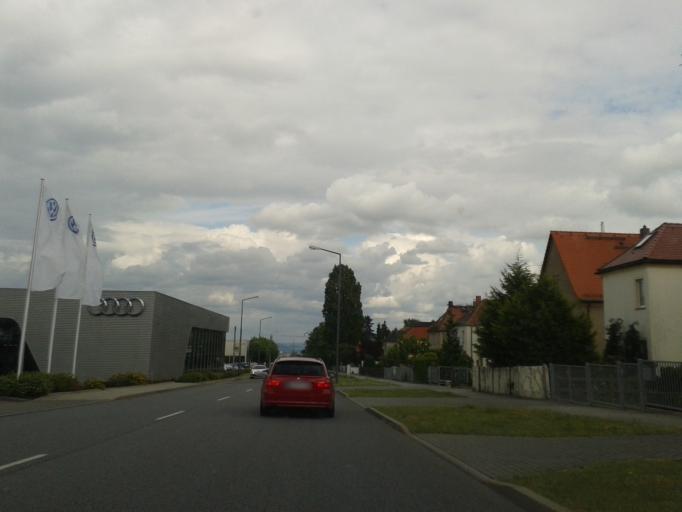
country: DE
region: Saxony
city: Freital
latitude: 51.0398
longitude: 13.6479
